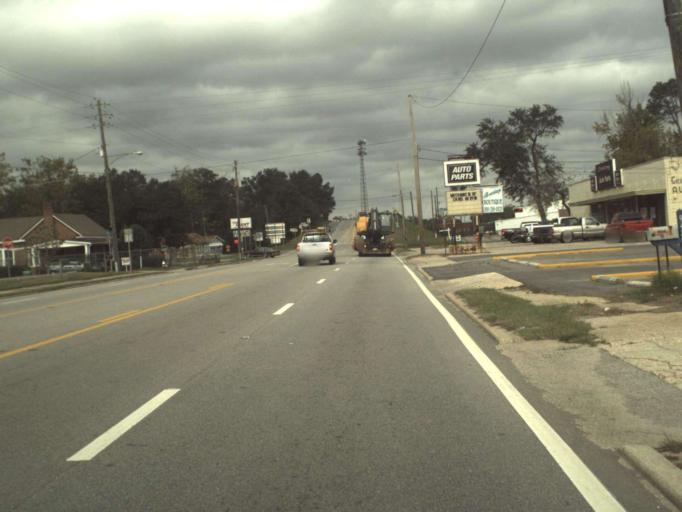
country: US
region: Alabama
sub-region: Escambia County
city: Flomaton
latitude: 30.9959
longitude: -87.2591
